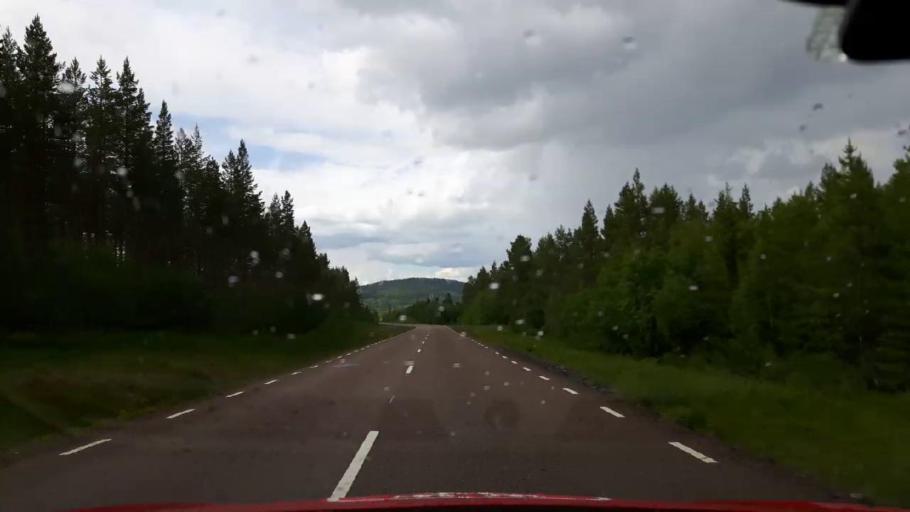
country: SE
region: Jaemtland
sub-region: Krokoms Kommun
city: Valla
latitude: 63.8938
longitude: 14.2611
